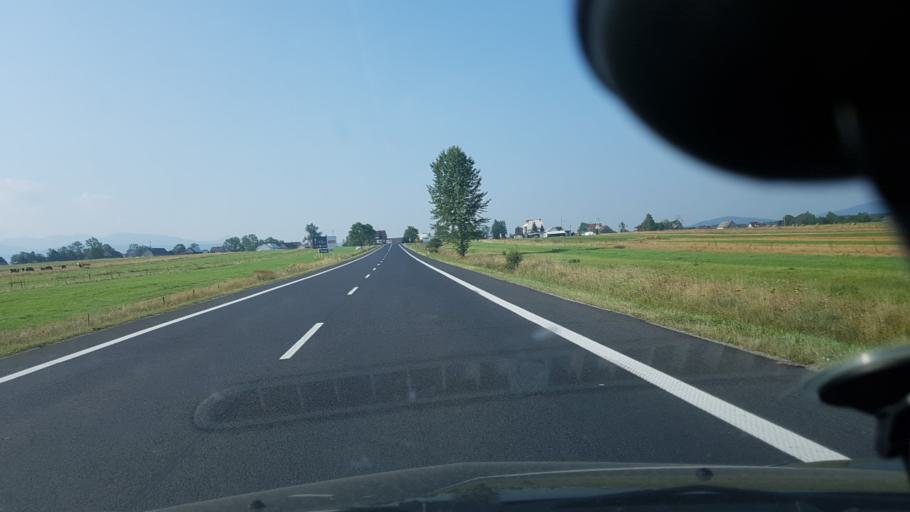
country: PL
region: Lesser Poland Voivodeship
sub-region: Powiat nowotarski
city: Chyzne
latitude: 49.4316
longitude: 19.6774
